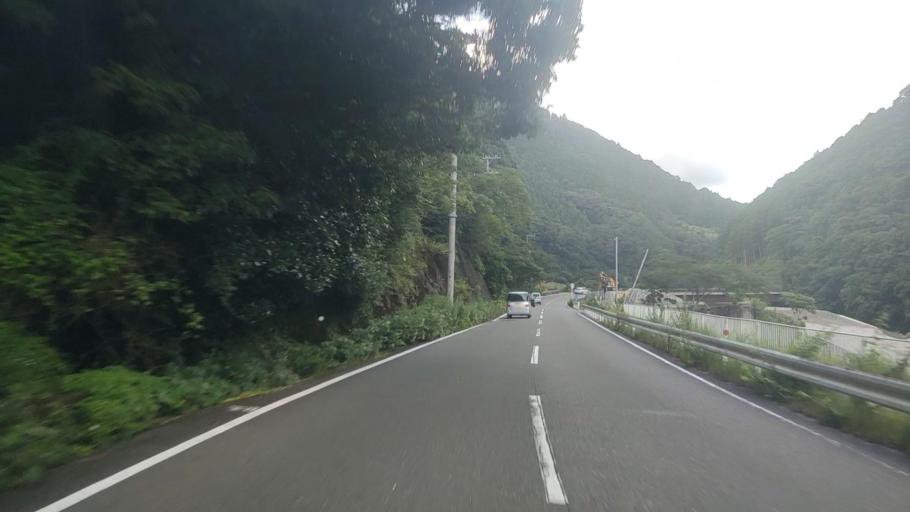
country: JP
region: Wakayama
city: Tanabe
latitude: 33.7704
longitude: 135.4998
